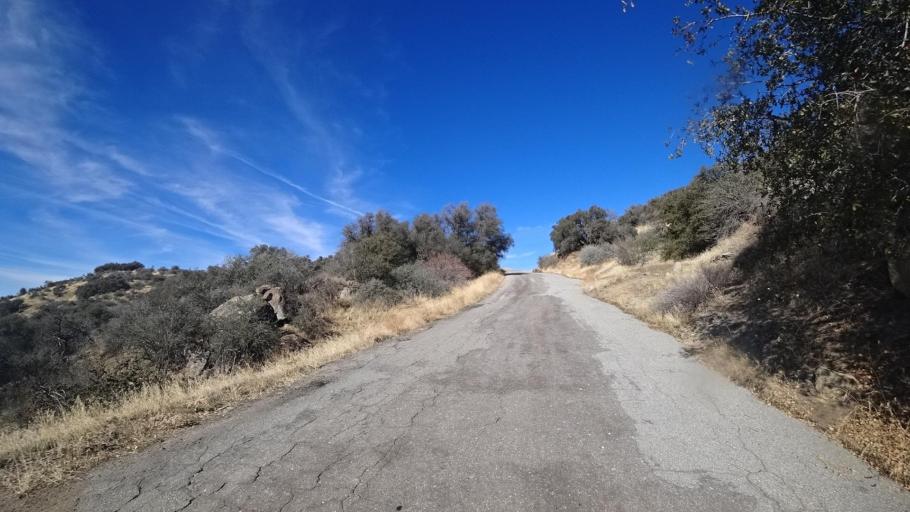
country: US
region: California
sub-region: Kern County
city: Bodfish
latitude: 35.4589
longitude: -118.6555
